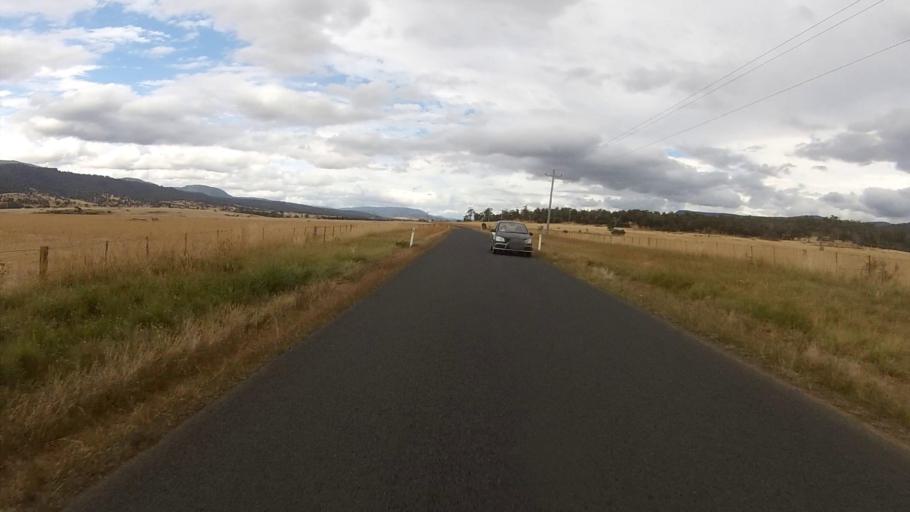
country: AU
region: Tasmania
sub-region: Northern Midlands
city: Evandale
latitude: -41.8254
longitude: 147.8029
